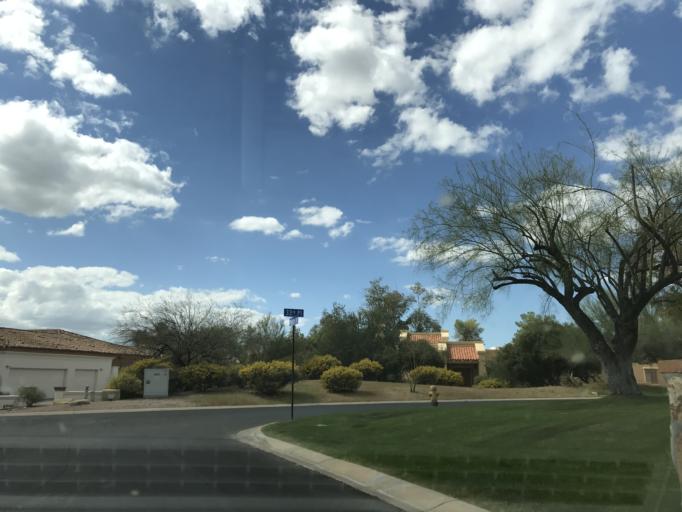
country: US
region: Arizona
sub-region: Maricopa County
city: Paradise Valley
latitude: 33.5227
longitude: -112.0091
